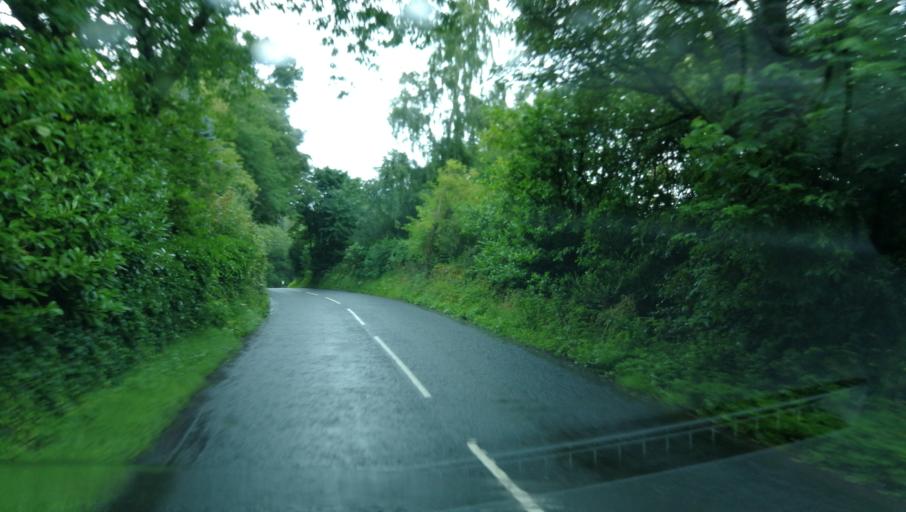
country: GB
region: England
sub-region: Cumbria
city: Penrith
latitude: 54.5952
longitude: -2.8591
